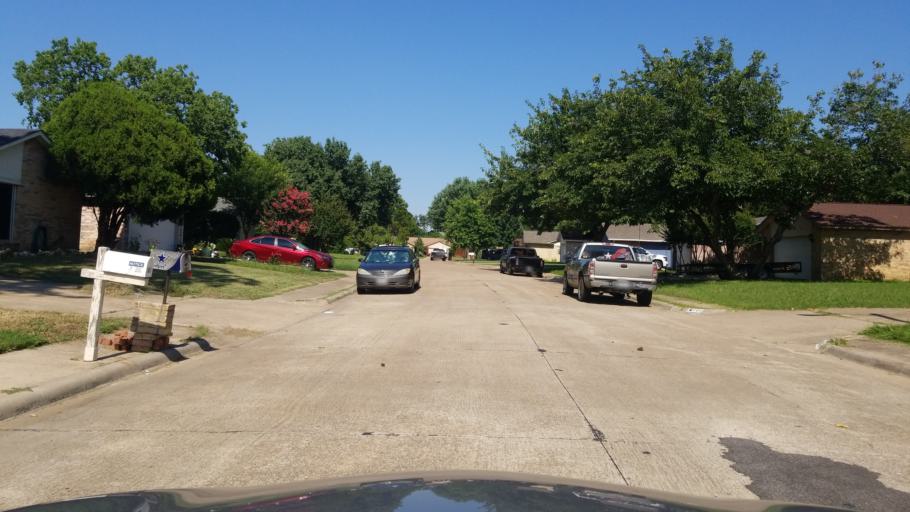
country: US
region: Texas
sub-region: Dallas County
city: Grand Prairie
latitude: 32.6794
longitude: -97.0130
